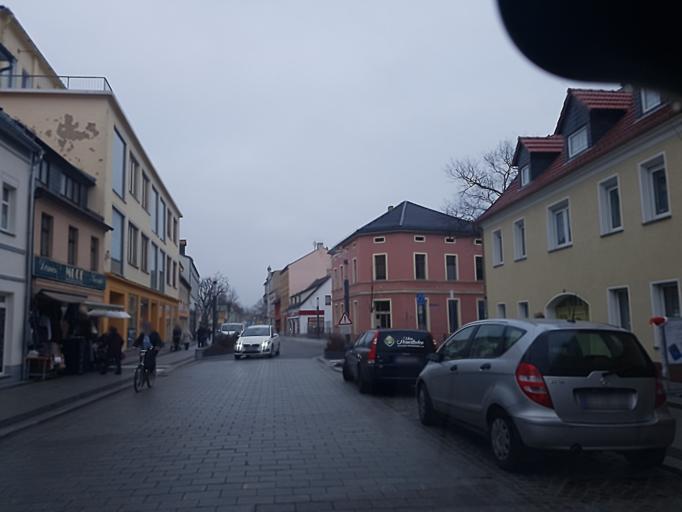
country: DE
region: Brandenburg
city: Finsterwalde
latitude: 51.6328
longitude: 13.7083
